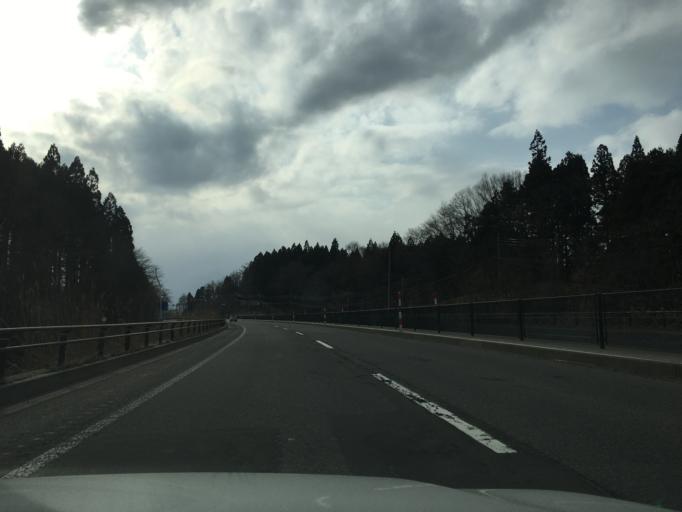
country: JP
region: Aomori
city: Aomori Shi
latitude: 40.8351
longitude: 140.6765
